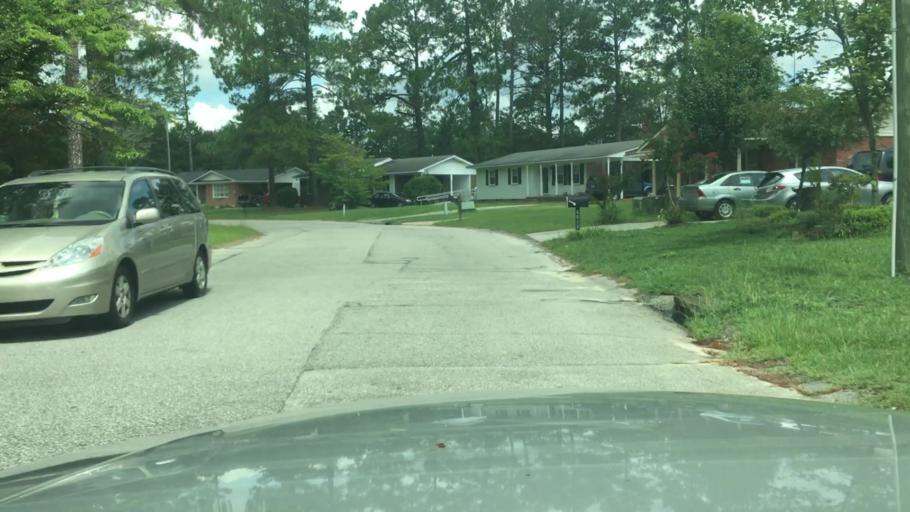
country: US
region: North Carolina
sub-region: Cumberland County
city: Hope Mills
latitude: 35.0387
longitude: -78.9802
